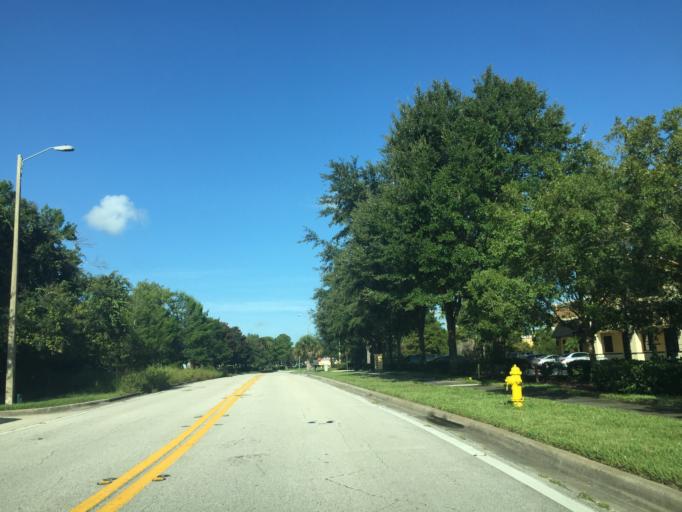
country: US
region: Florida
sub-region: Seminole County
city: Goldenrod
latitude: 28.6448
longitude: -81.2697
